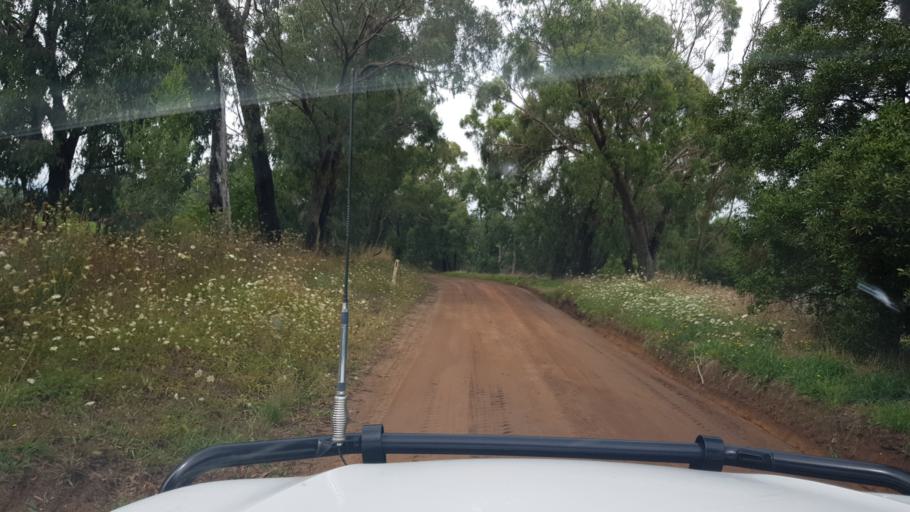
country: AU
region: Victoria
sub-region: Latrobe
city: Moe
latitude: -38.0726
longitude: 146.1451
